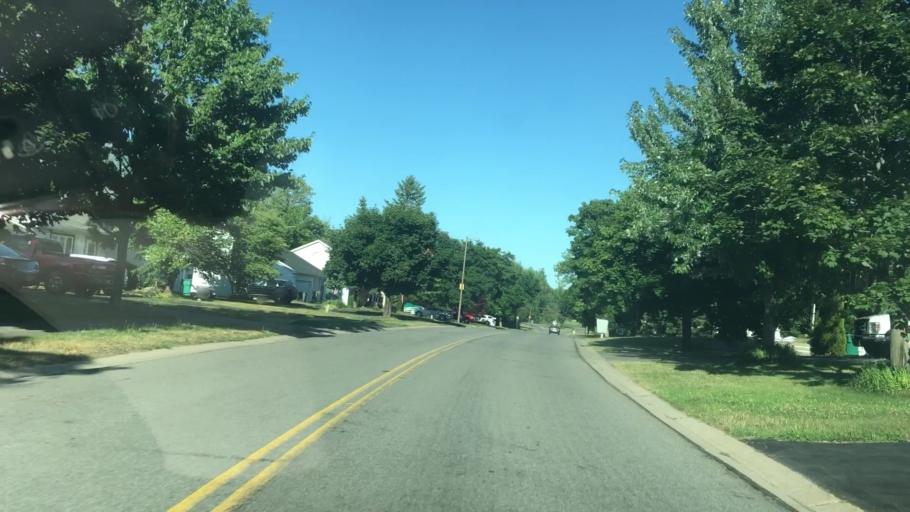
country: US
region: New York
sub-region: Wayne County
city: Macedon
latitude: 43.1280
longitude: -77.2962
